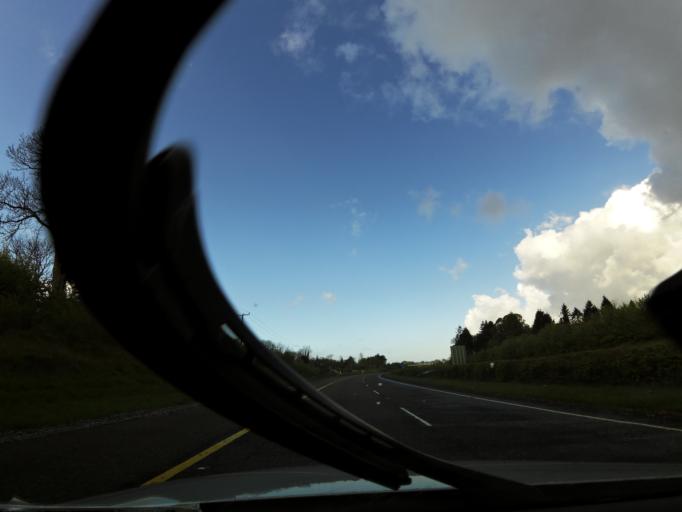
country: IE
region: Munster
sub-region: County Limerick
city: Annacotty
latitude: 52.6612
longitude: -8.5232
